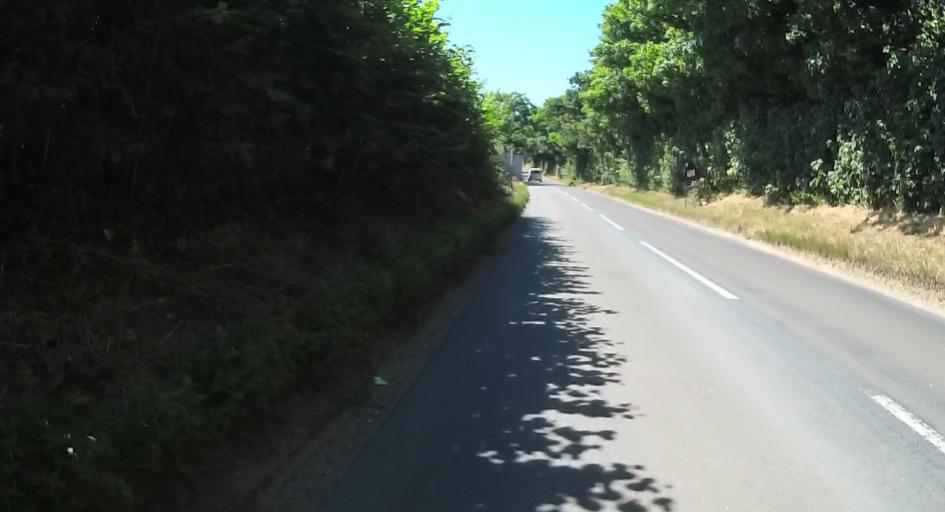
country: GB
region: England
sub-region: Dorset
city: Wool
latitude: 50.6366
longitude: -2.2195
